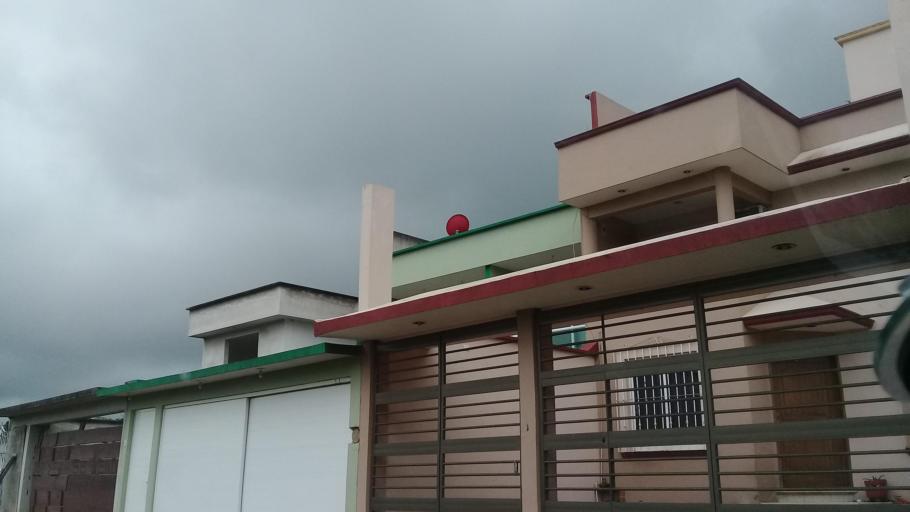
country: MX
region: Veracruz
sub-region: Xalapa
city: Colonia Santa Barbara
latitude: 19.4964
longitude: -96.8702
